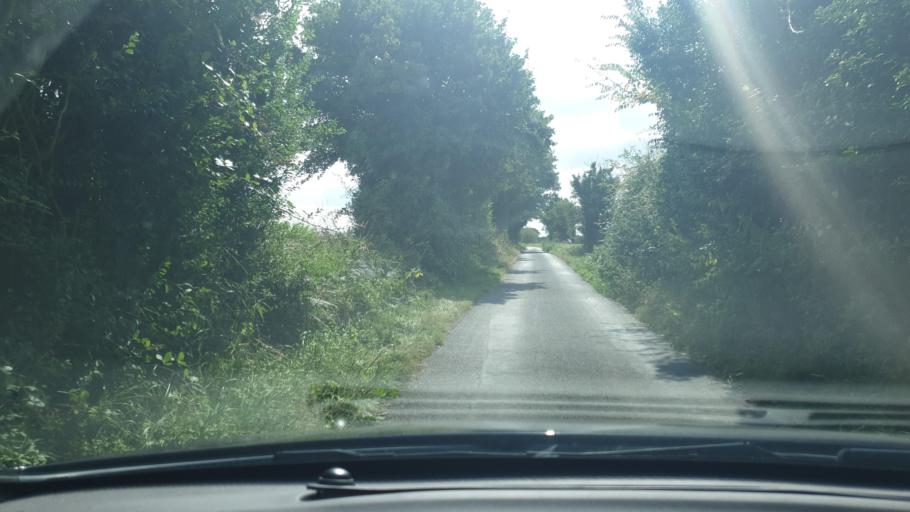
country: GB
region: England
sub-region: Essex
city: Manningtree
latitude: 51.9293
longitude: 1.0317
